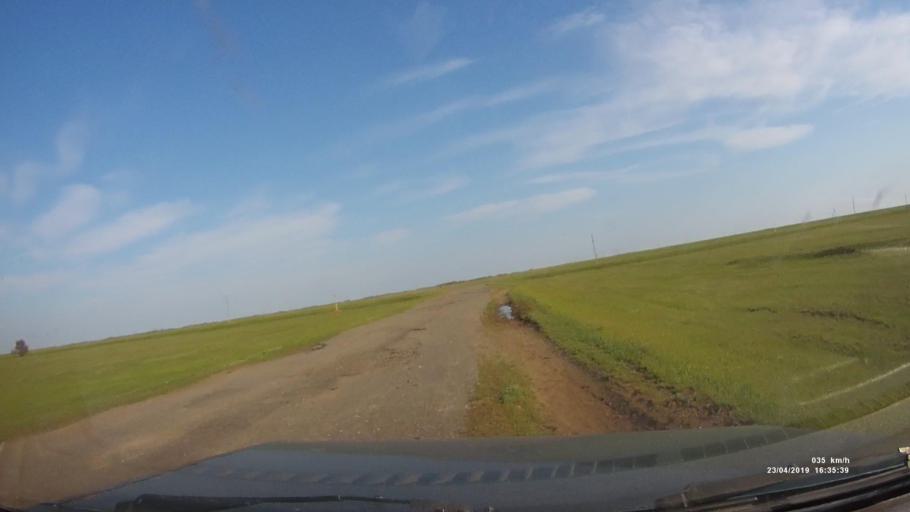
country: RU
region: Kalmykiya
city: Priyutnoye
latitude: 46.3298
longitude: 43.1385
